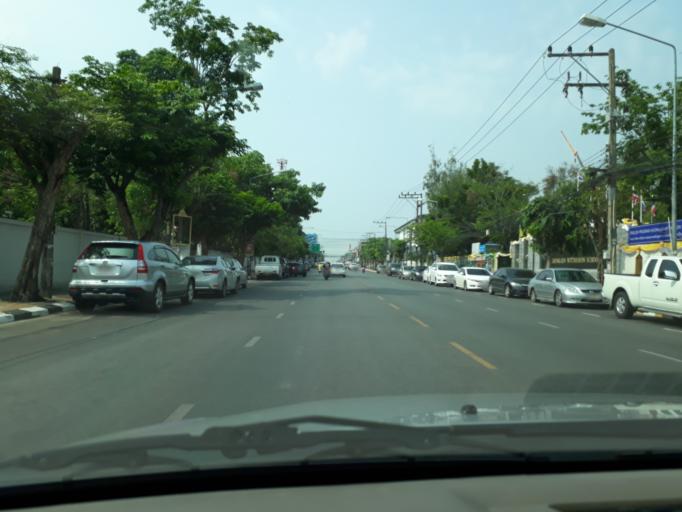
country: TH
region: Khon Kaen
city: Khon Kaen
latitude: 16.4323
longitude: 102.8361
